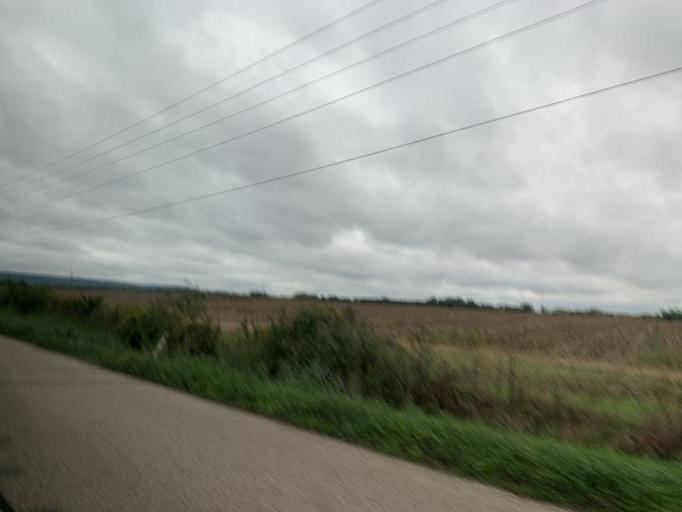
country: US
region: Wisconsin
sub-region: Sauk County
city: Prairie du Sac
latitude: 43.3384
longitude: -89.7668
